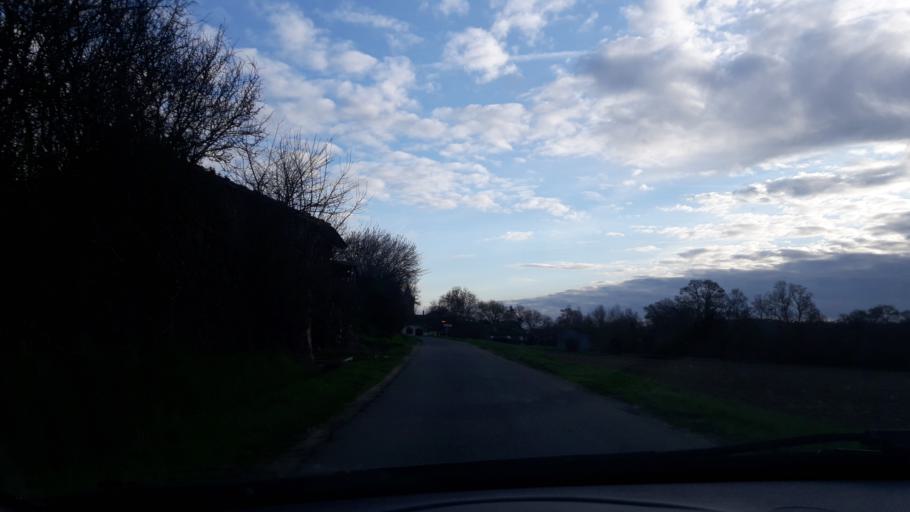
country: FR
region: Midi-Pyrenees
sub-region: Departement de la Haute-Garonne
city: Levignac
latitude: 43.6605
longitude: 1.1650
